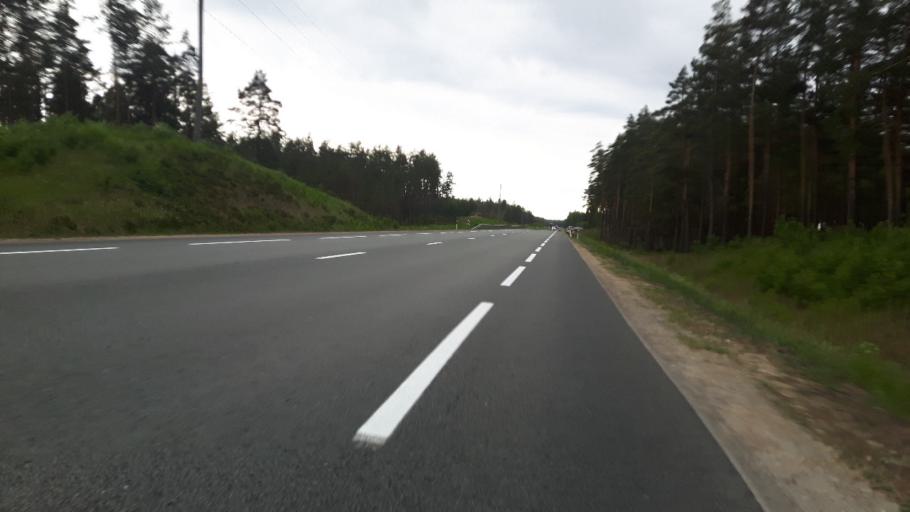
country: LV
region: Saulkrastu
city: Saulkrasti
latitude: 57.2112
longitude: 24.3922
